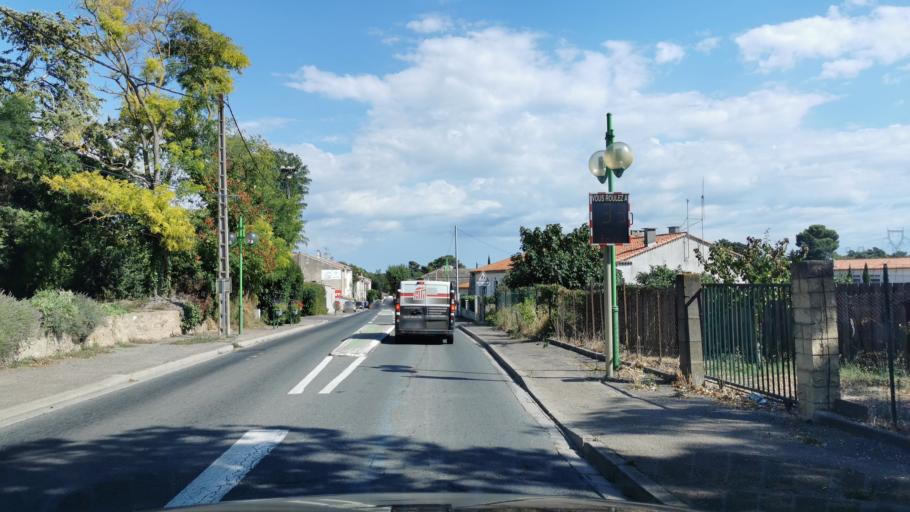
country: FR
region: Languedoc-Roussillon
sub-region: Departement de l'Aude
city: Azille
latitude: 43.2529
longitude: 2.6486
